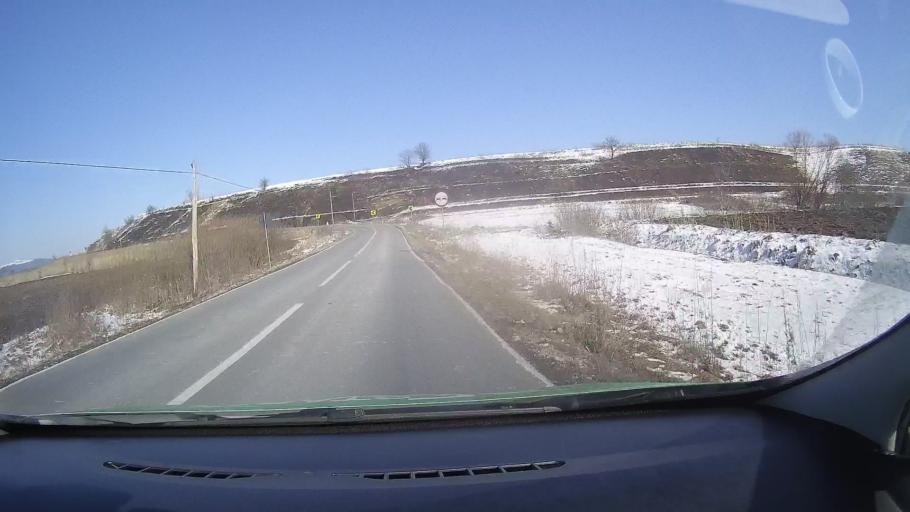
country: RO
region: Brasov
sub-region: Comuna Comana
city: Comana de Jos
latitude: 45.8982
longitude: 25.2274
